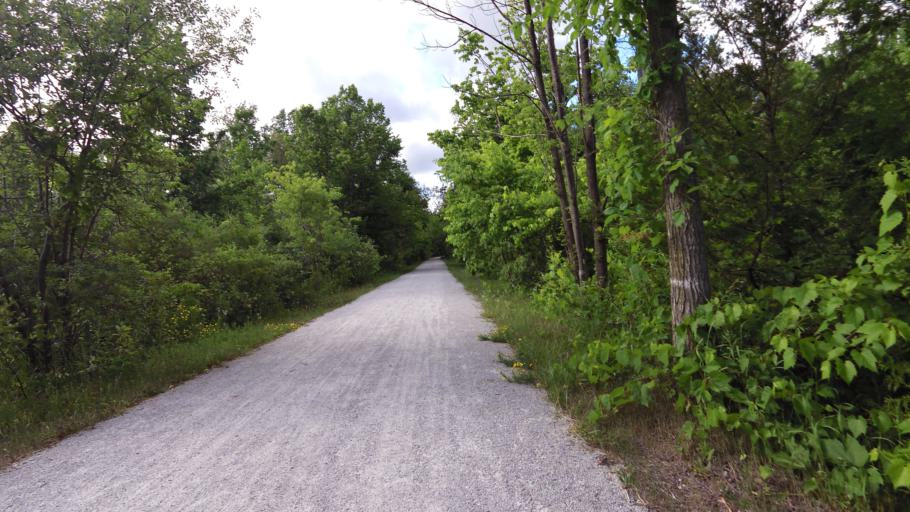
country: CA
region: Ontario
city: Orangeville
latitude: 43.8065
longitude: -79.9325
